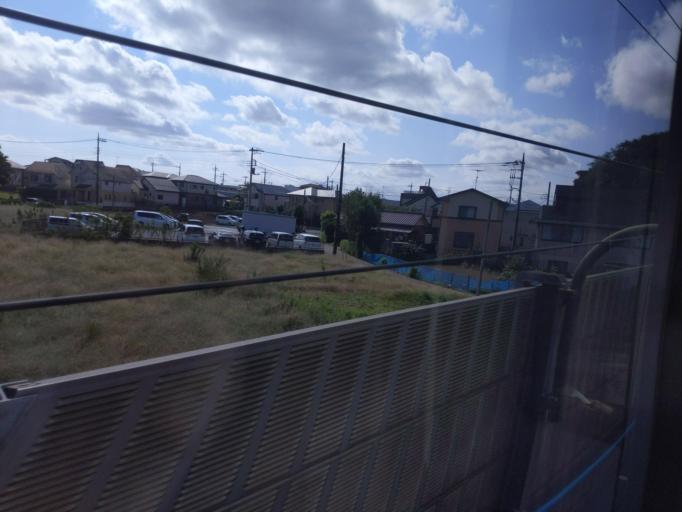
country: JP
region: Chiba
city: Shiroi
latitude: 35.7266
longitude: 140.1085
